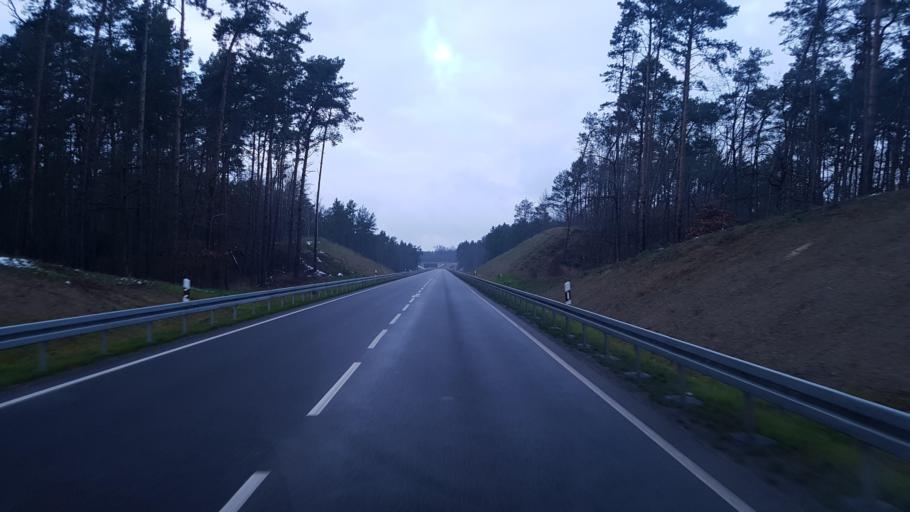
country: DE
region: Brandenburg
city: Wildau
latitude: 52.3168
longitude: 13.6602
